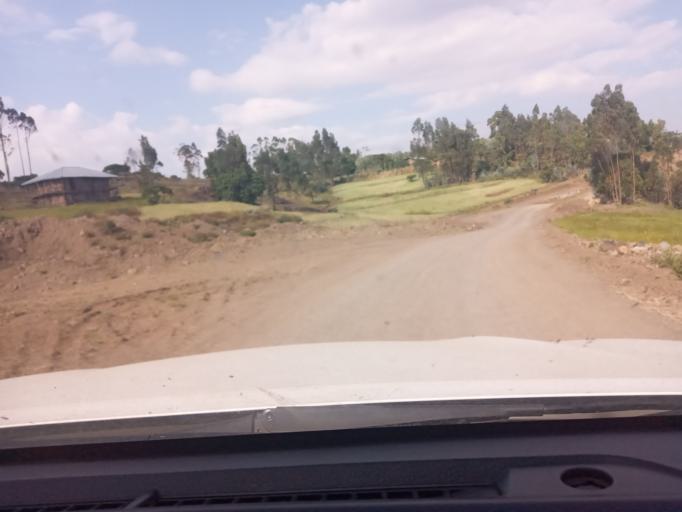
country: ET
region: Amhara
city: Were Ilu
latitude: 10.6139
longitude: 39.0404
